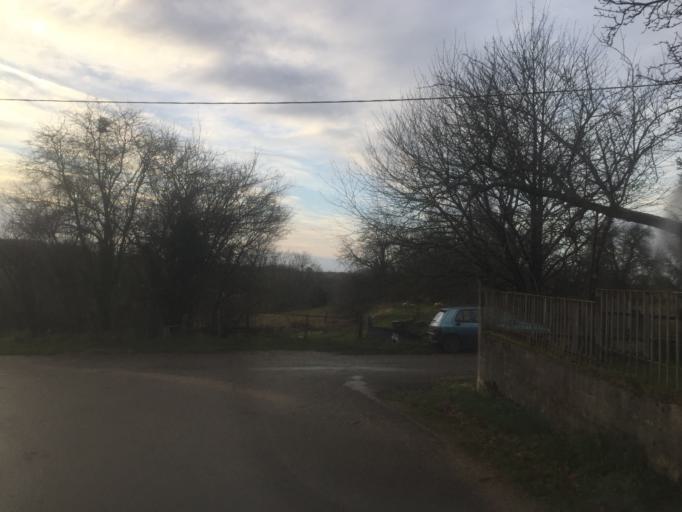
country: FR
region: Franche-Comte
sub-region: Departement du Jura
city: Orchamps
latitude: 47.1286
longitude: 5.6680
